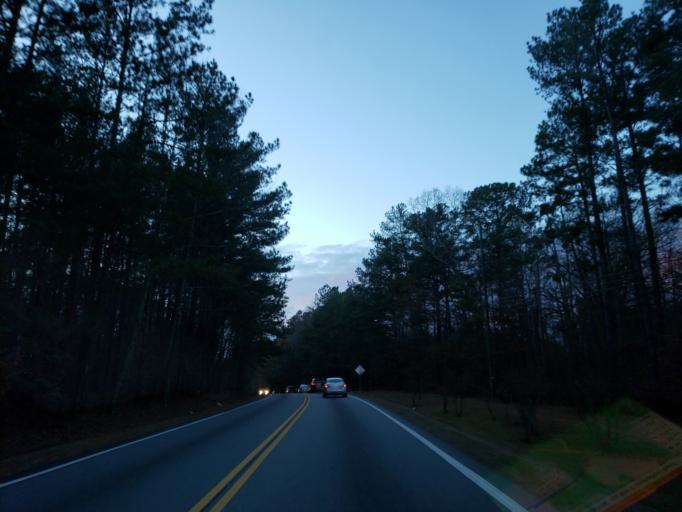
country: US
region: Georgia
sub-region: Douglas County
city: Lithia Springs
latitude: 33.6923
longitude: -84.6153
